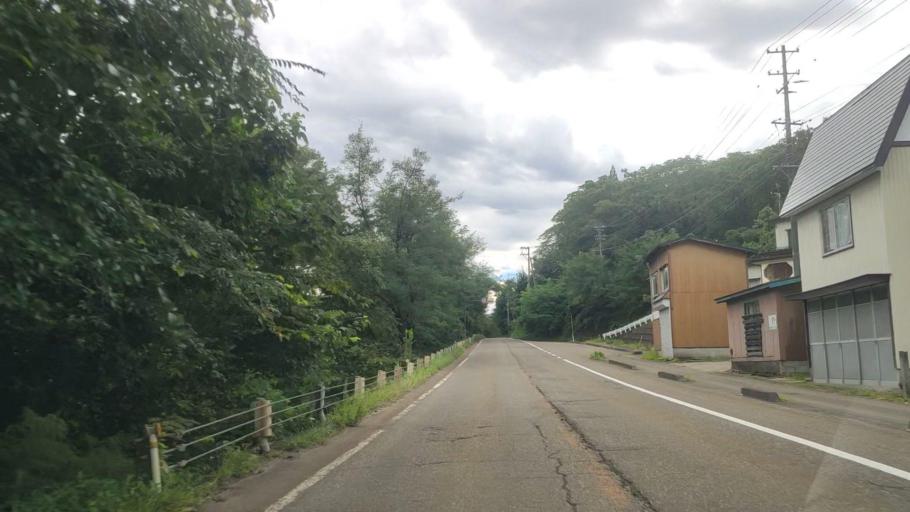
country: JP
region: Niigata
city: Arai
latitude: 36.9980
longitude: 138.2671
